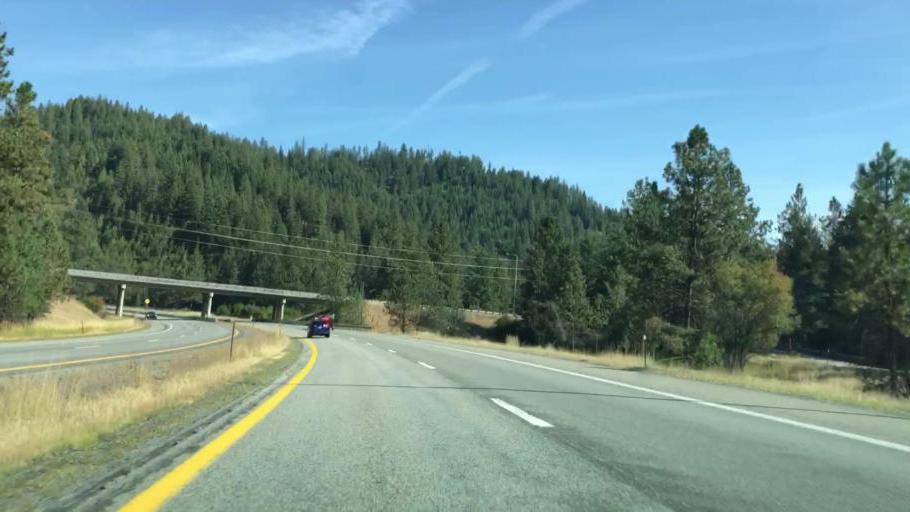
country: US
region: Idaho
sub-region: Shoshone County
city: Pinehurst
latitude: 47.5749
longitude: -116.4447
